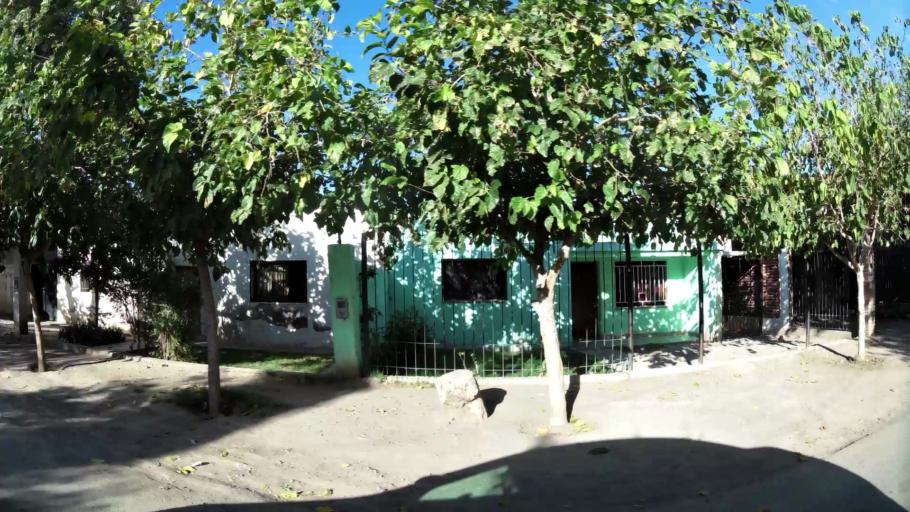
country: AR
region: San Juan
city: Villa Krause
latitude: -31.5527
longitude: -68.5158
